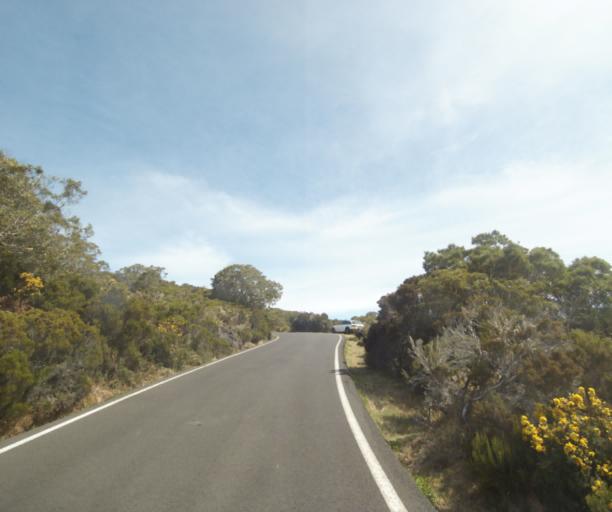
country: RE
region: Reunion
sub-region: Reunion
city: Trois-Bassins
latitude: -21.0636
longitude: 55.3785
